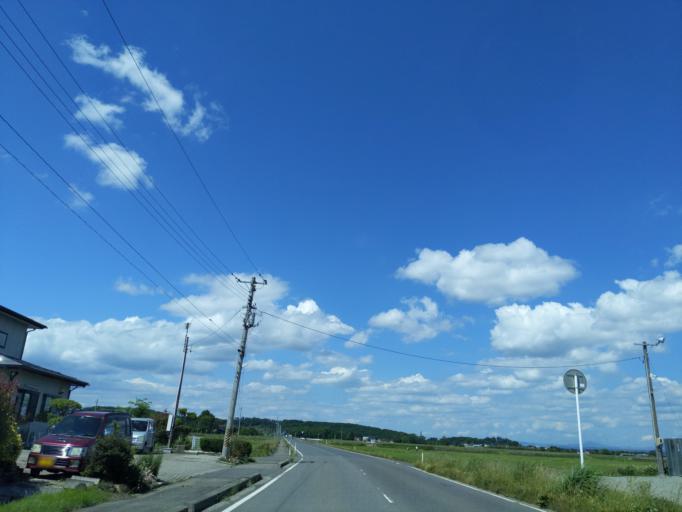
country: JP
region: Fukushima
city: Koriyama
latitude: 37.3814
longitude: 140.2973
